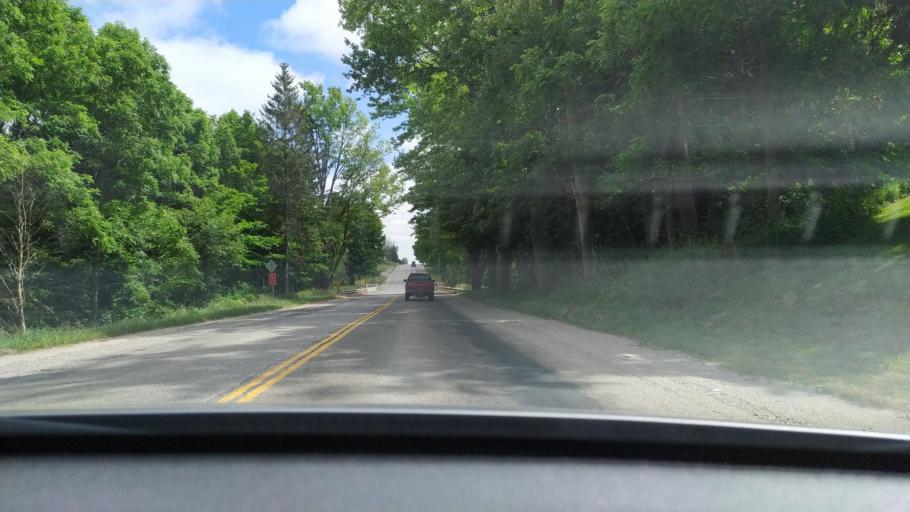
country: CA
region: Ontario
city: Stratford
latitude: 43.2967
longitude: -80.9736
